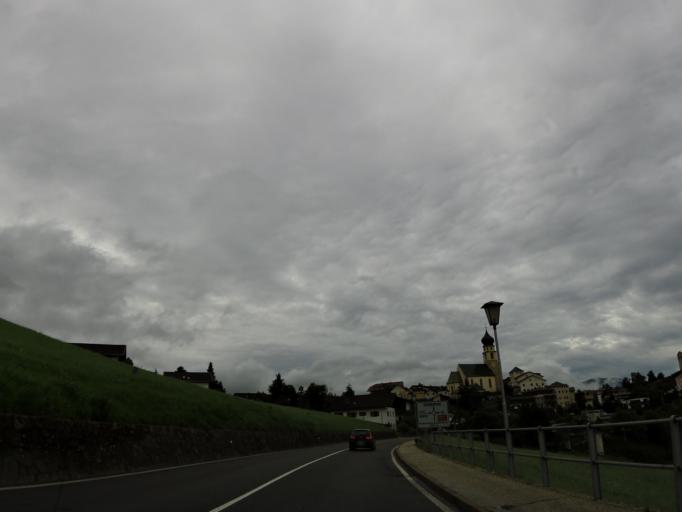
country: IT
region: Trentino-Alto Adige
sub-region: Bolzano
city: Fie Allo Sciliar
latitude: 46.5201
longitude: 11.5062
